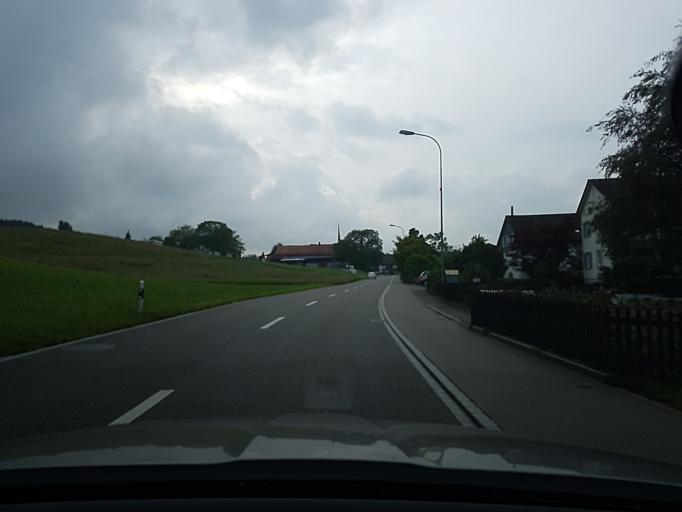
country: CH
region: Thurgau
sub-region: Arbon District
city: Roggwil
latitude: 47.4987
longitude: 9.4022
